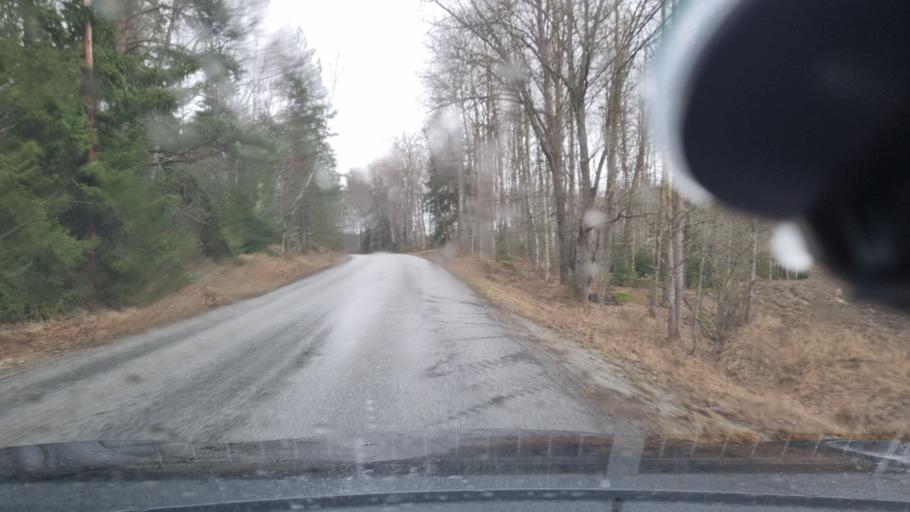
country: SE
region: Stockholm
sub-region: Sigtuna Kommun
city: Sigtuna
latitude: 59.5662
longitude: 17.6899
